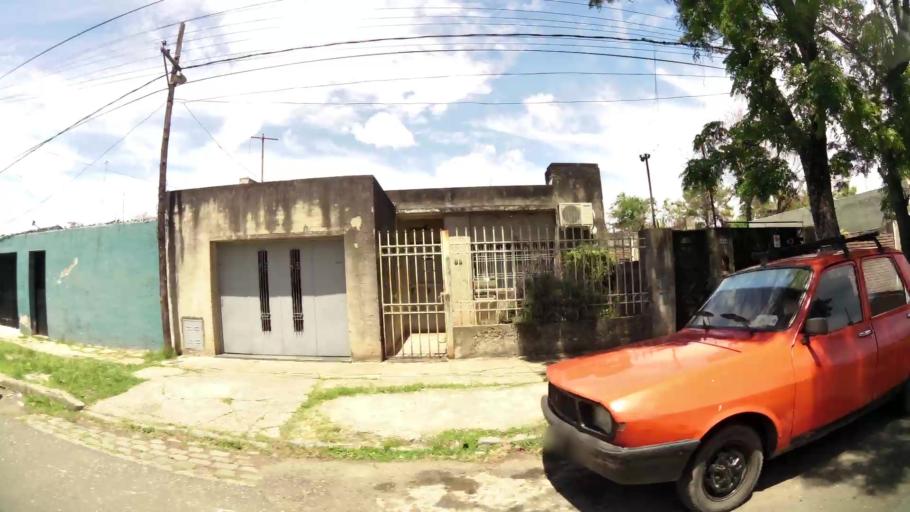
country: AR
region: Santa Fe
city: Gobernador Galvez
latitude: -32.9963
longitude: -60.6219
